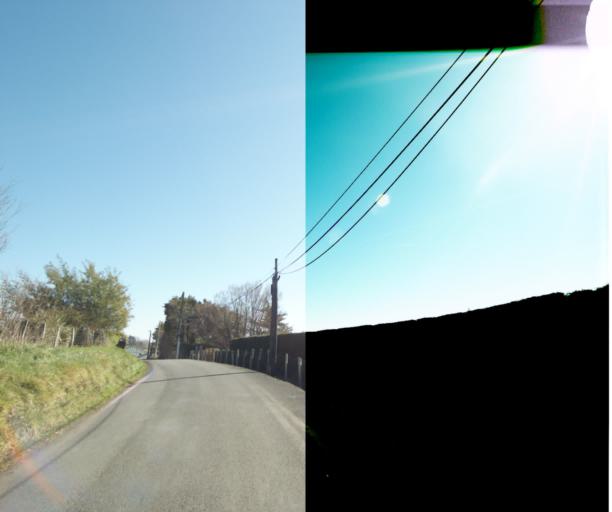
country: FR
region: Aquitaine
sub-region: Departement des Pyrenees-Atlantiques
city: Urrugne
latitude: 43.3483
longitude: -1.6718
